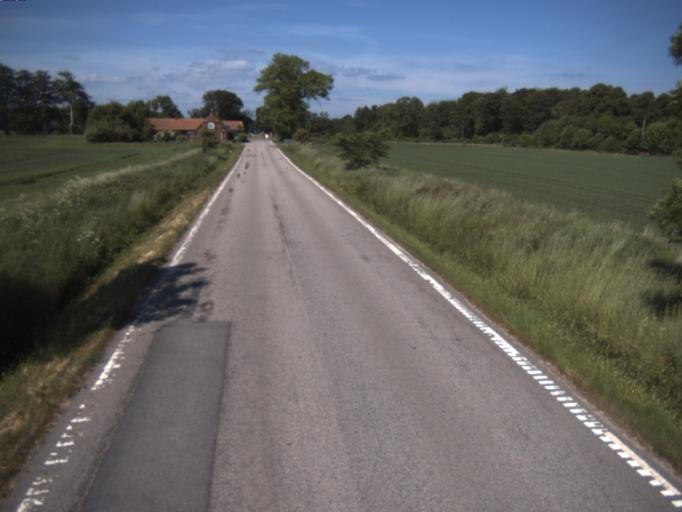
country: DK
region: Capital Region
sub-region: Helsingor Kommune
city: Helsingor
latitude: 56.1069
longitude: 12.6418
